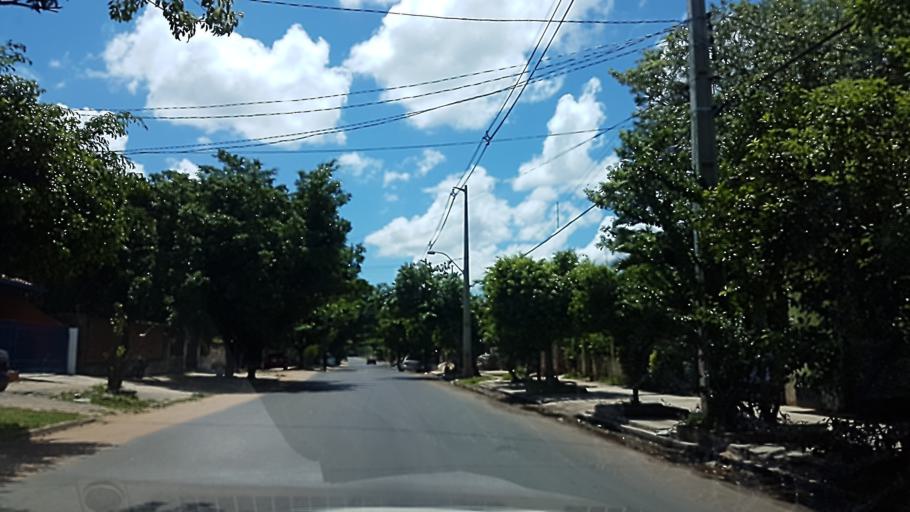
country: PY
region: Central
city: Colonia Mariano Roque Alonso
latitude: -25.2461
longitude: -57.5325
